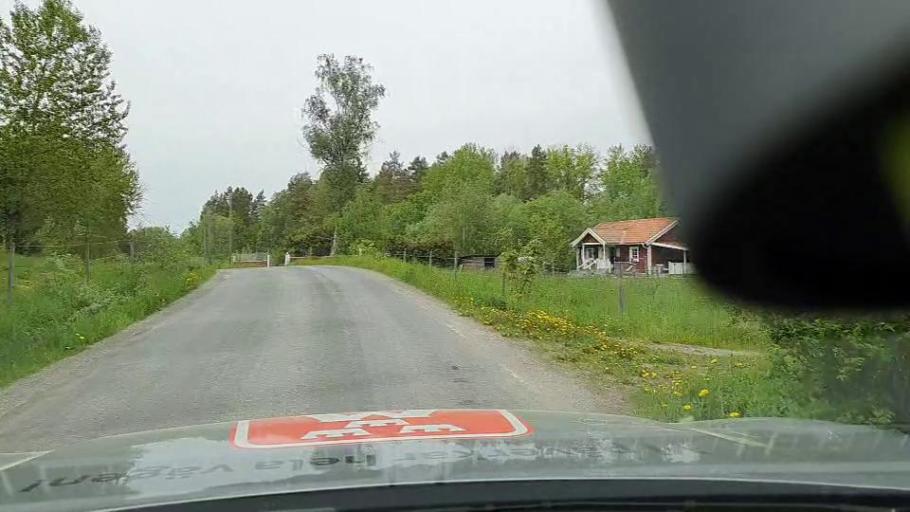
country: SE
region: Soedermanland
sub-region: Flens Kommun
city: Flen
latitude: 59.1039
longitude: 16.5452
